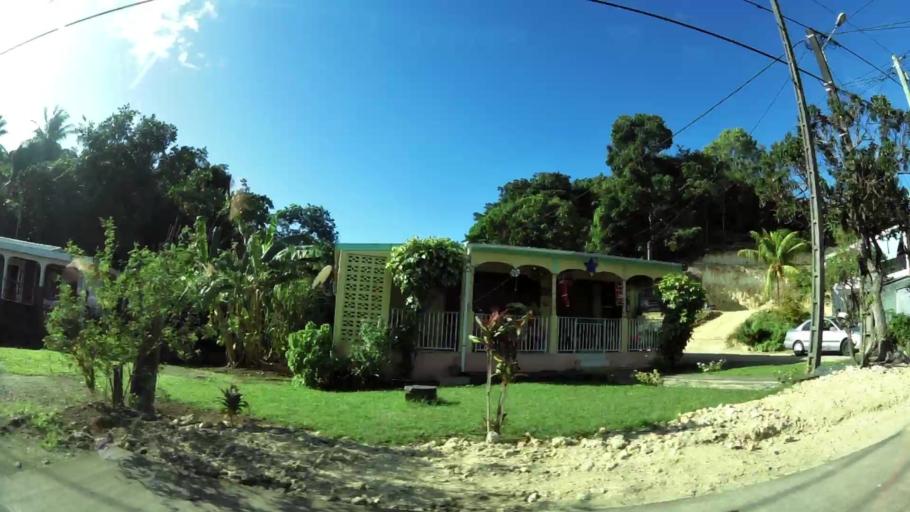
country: GP
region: Guadeloupe
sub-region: Guadeloupe
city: Petit-Canal
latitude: 16.3242
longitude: -61.4431
